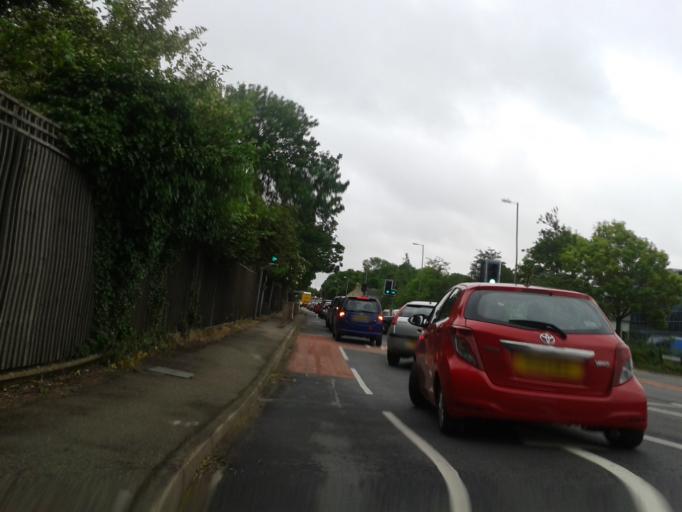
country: GB
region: England
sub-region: Cambridgeshire
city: Histon
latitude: 52.2456
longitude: 0.1107
